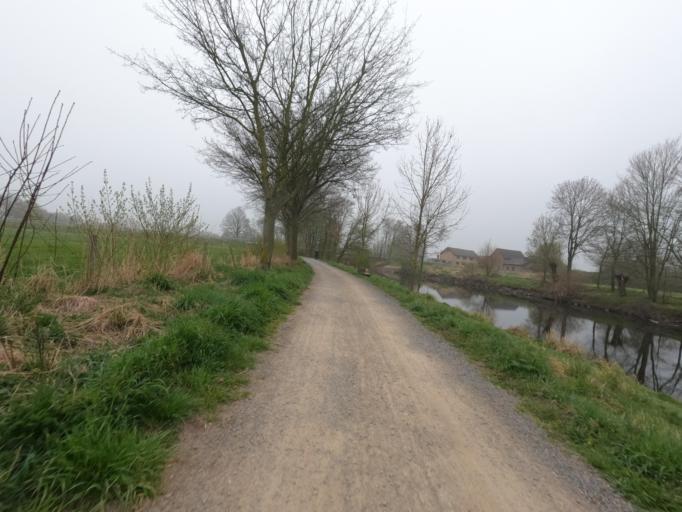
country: DE
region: North Rhine-Westphalia
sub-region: Regierungsbezirk Koln
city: Heinsberg
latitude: 51.0980
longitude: 6.1032
